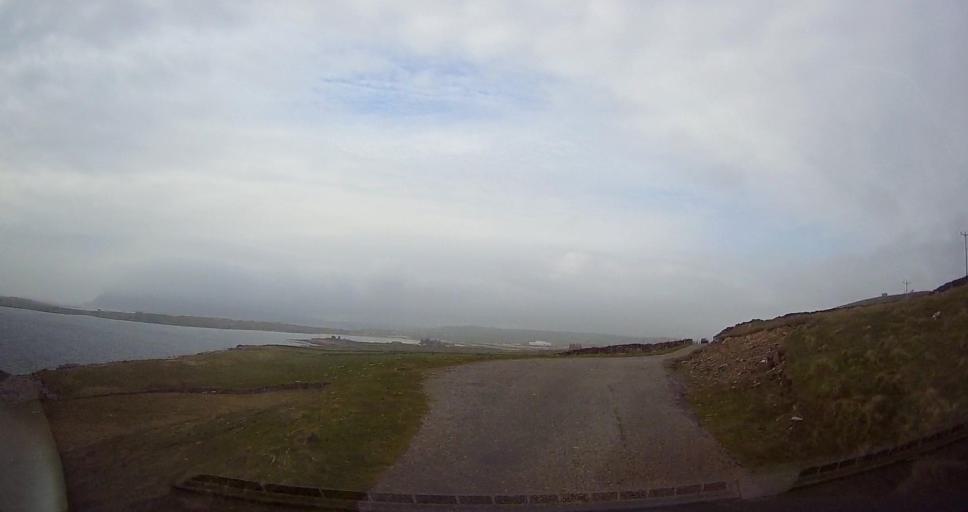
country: GB
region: Scotland
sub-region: Shetland Islands
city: Sandwick
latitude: 59.8599
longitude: -1.2780
